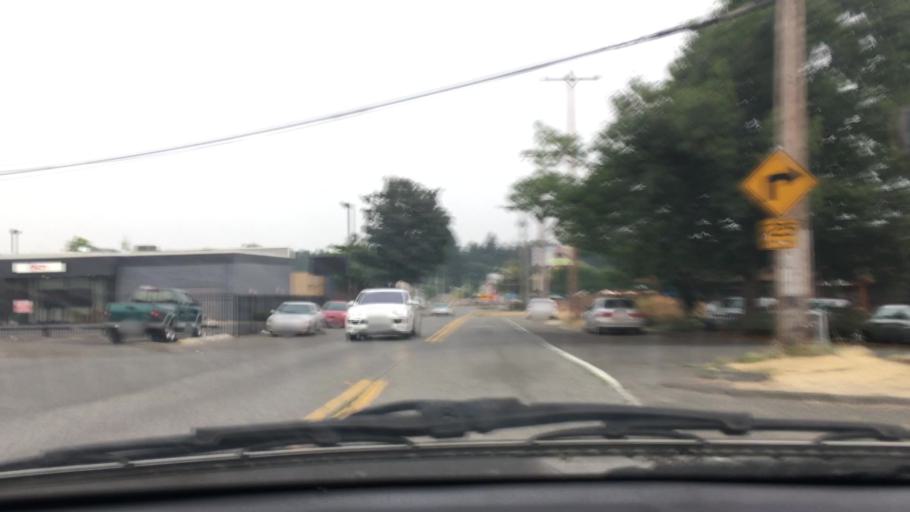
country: US
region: Washington
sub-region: King County
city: Burien
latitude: 47.4616
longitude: -122.3361
